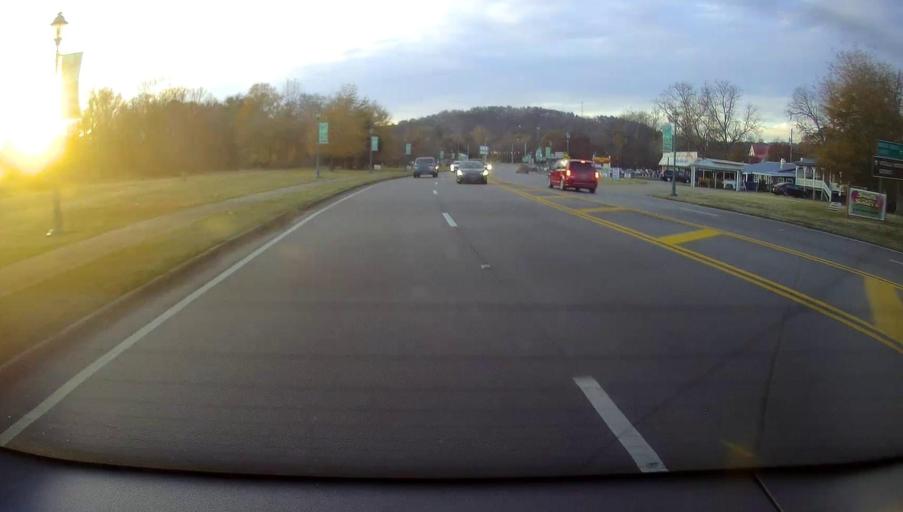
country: US
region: Alabama
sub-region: Etowah County
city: Attalla
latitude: 34.0190
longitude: -86.0835
